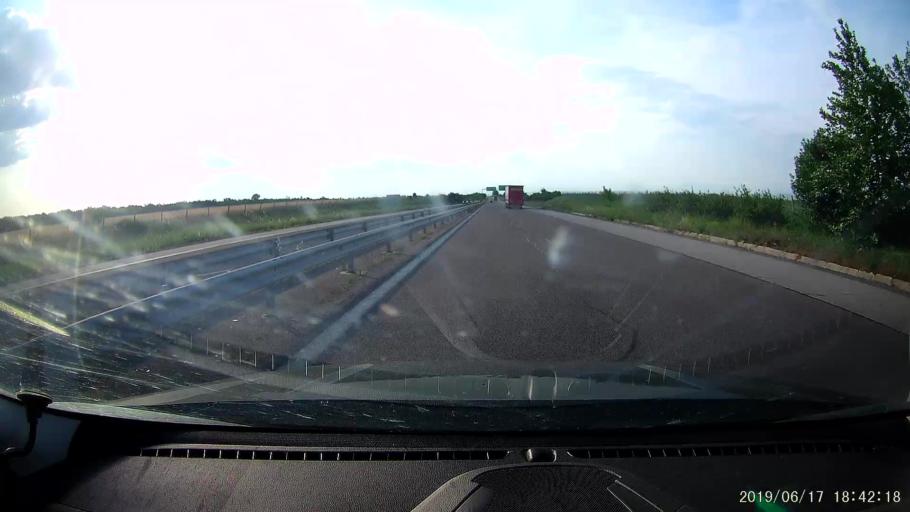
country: BG
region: Stara Zagora
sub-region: Obshtina Chirpan
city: Chirpan
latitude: 42.1889
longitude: 25.2395
